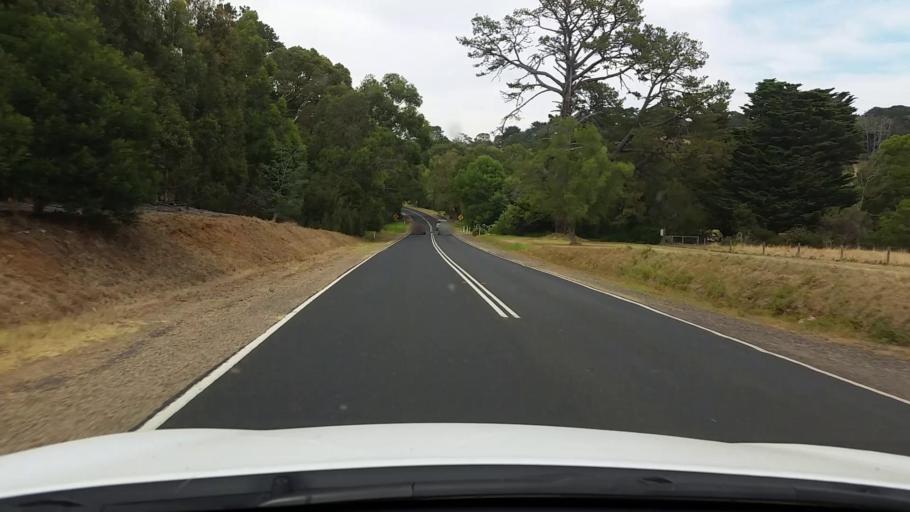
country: AU
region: Victoria
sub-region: Mornington Peninsula
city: Merricks
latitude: -38.4271
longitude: 145.0427
